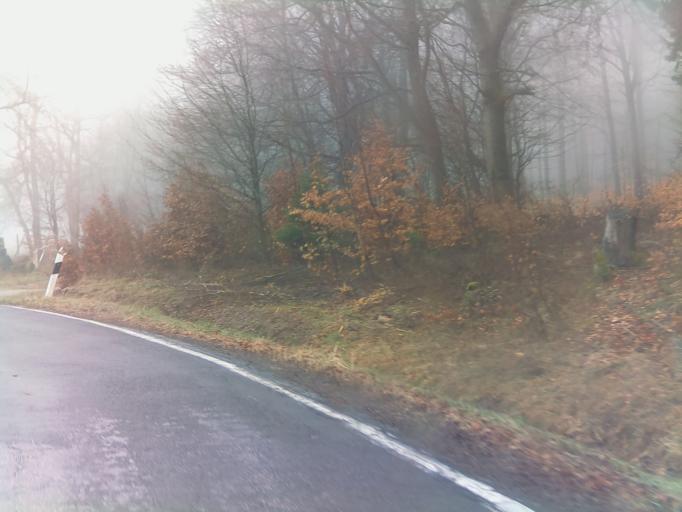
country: DE
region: Rheinland-Pfalz
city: Tiefenbach
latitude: 49.9177
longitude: 7.5761
